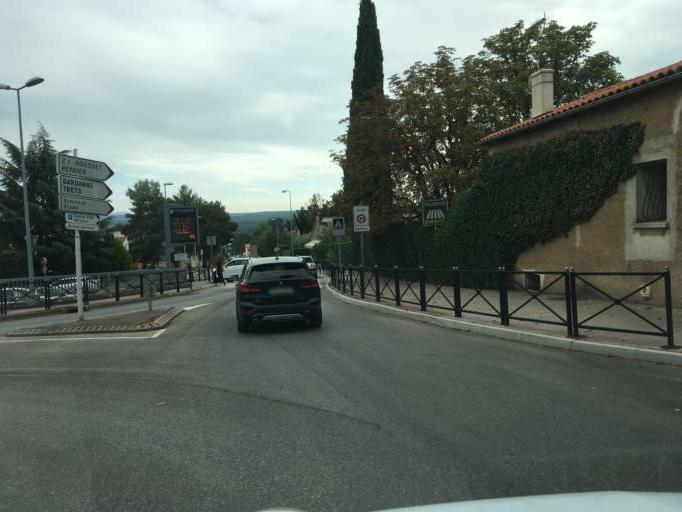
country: FR
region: Provence-Alpes-Cote d'Azur
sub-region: Departement des Bouches-du-Rhone
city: Rousset
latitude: 43.4826
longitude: 5.6239
